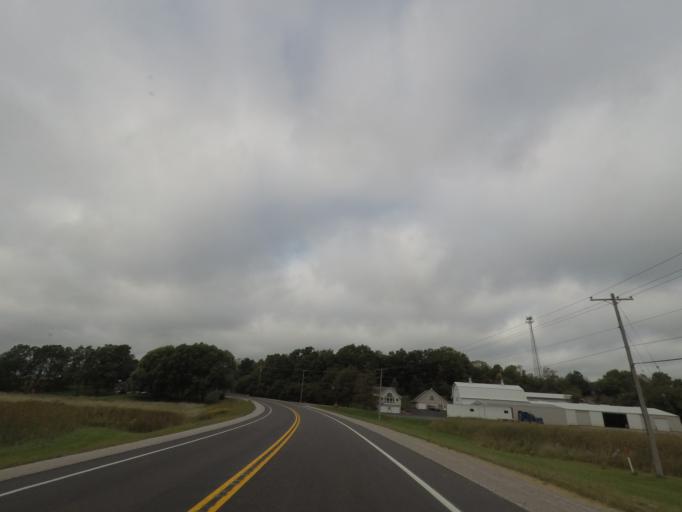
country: US
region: Wisconsin
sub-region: Jefferson County
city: Jefferson
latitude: 43.0128
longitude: -88.7602
